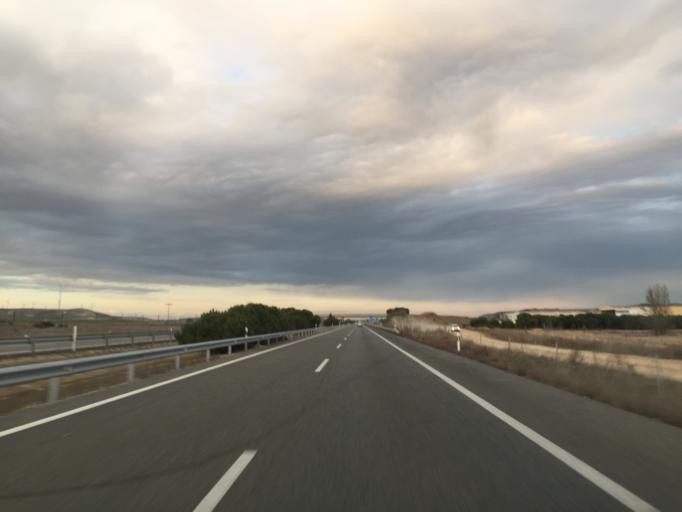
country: ES
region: Castille and Leon
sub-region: Provincia de Burgos
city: Villazopeque
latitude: 42.1949
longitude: -4.0280
